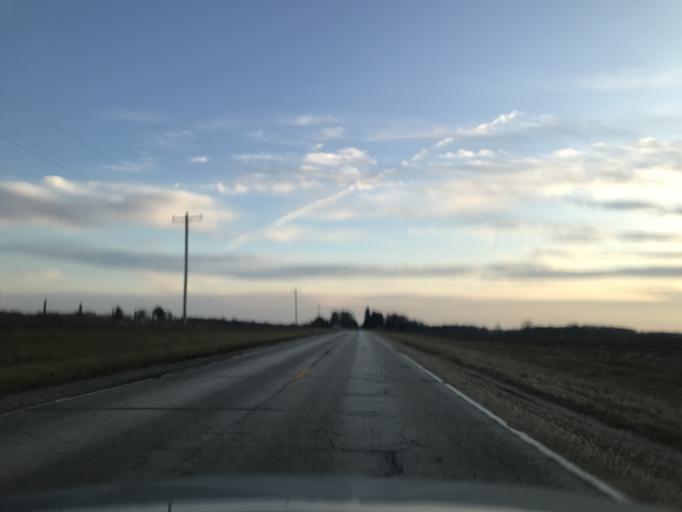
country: US
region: Illinois
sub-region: Henderson County
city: Oquawka
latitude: 40.9475
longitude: -90.8641
